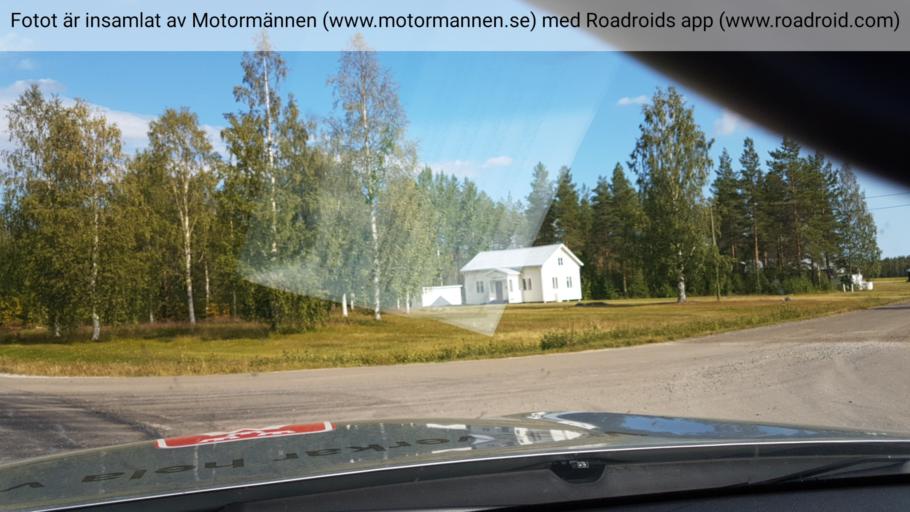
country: SE
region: Vaesterbotten
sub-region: Skelleftea Kommun
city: Backa
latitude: 65.1854
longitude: 21.0609
